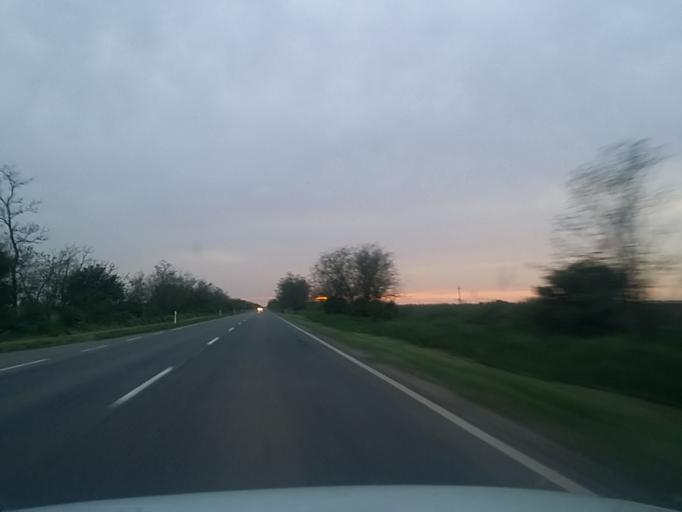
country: HU
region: Bekes
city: Bekescsaba
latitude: 46.7085
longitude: 20.9899
